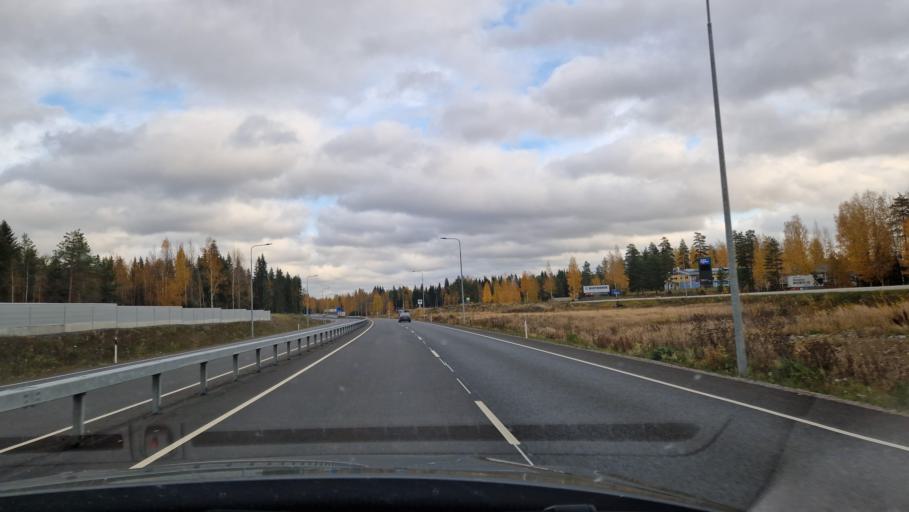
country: FI
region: Southern Savonia
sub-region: Pieksaemaeki
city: Juva
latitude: 61.8866
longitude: 27.7915
